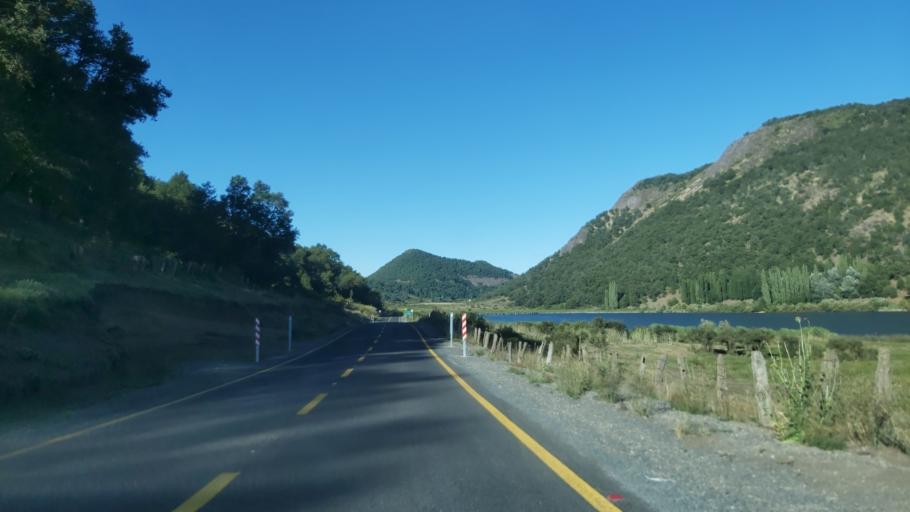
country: AR
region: Neuquen
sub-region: Departamento de Loncopue
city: Loncopue
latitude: -38.4421
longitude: -71.3385
